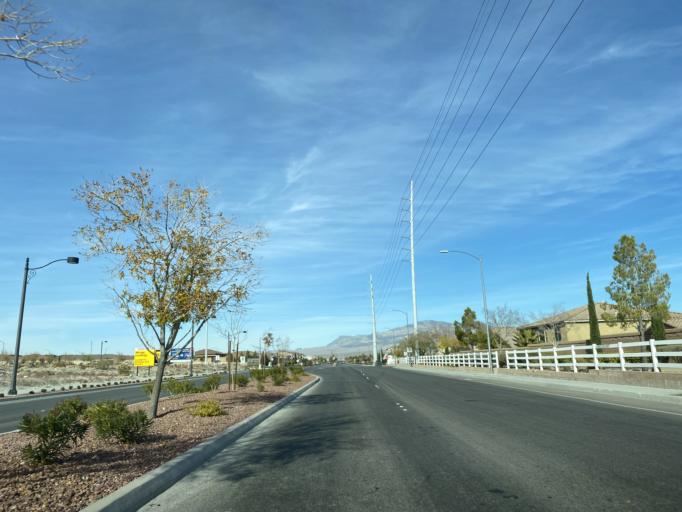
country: US
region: Nevada
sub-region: Clark County
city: Summerlin South
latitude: 36.3052
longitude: -115.3148
